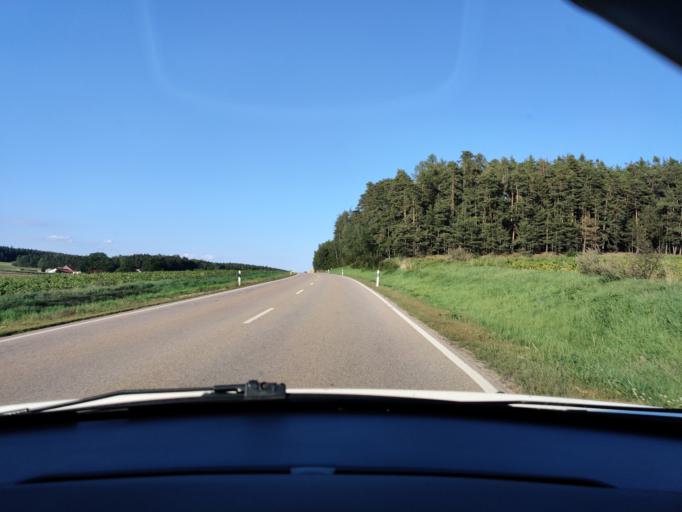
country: DE
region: Bavaria
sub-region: Upper Palatinate
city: Stulln
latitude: 49.4405
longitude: 12.1499
